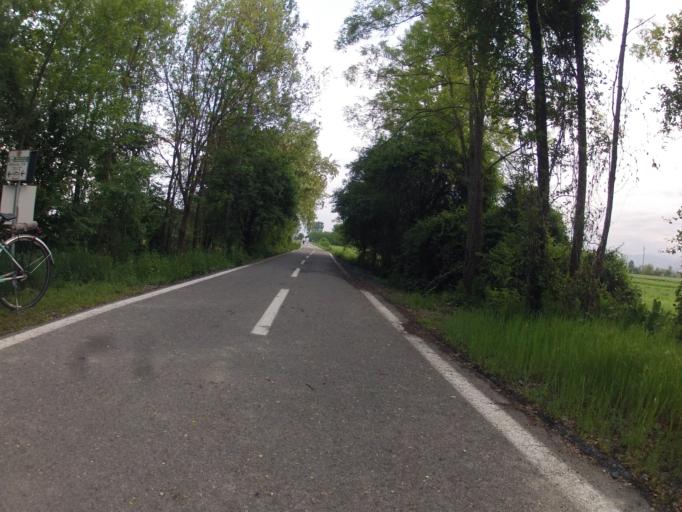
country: IT
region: Piedmont
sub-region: Provincia di Torino
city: Vigone
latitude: 44.8311
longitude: 7.4930
